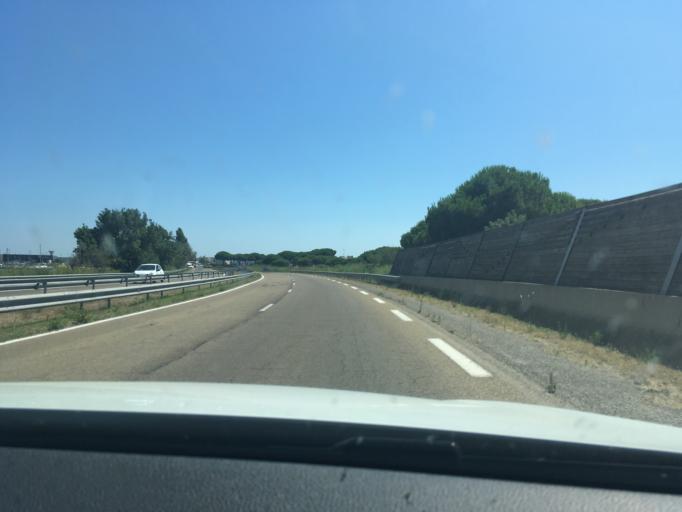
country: FR
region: Languedoc-Roussillon
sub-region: Departement du Gard
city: Le Grau-du-Roi
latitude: 43.5462
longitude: 4.1342
